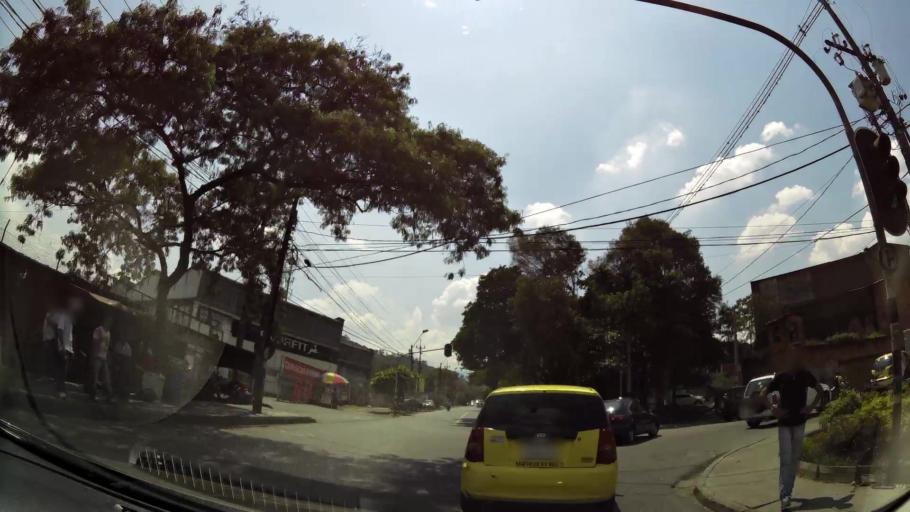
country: CO
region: Antioquia
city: Medellin
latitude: 6.2748
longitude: -75.5755
